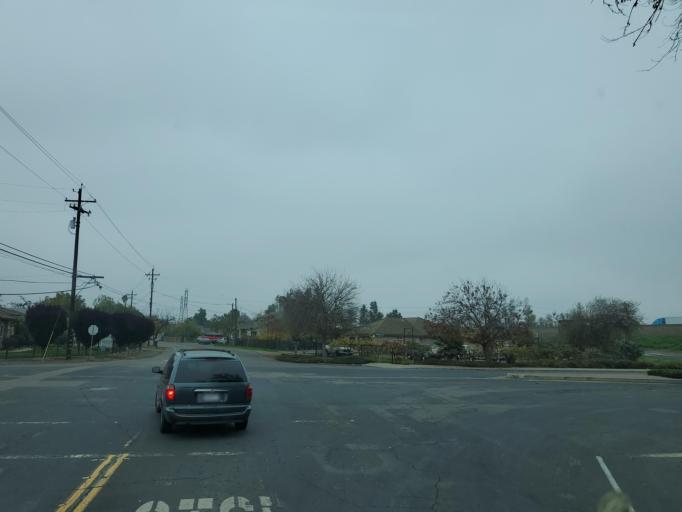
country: US
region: California
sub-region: San Joaquin County
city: Taft Mosswood
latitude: 37.9134
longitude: -121.2882
